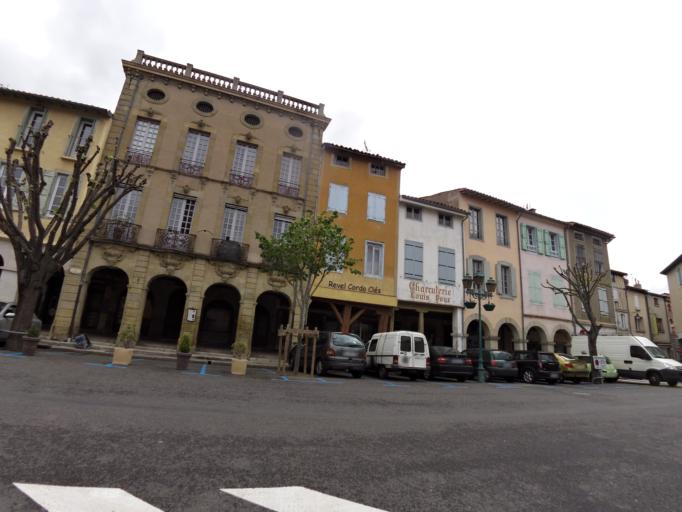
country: FR
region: Midi-Pyrenees
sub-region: Departement de la Haute-Garonne
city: Revel
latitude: 43.4587
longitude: 2.0047
